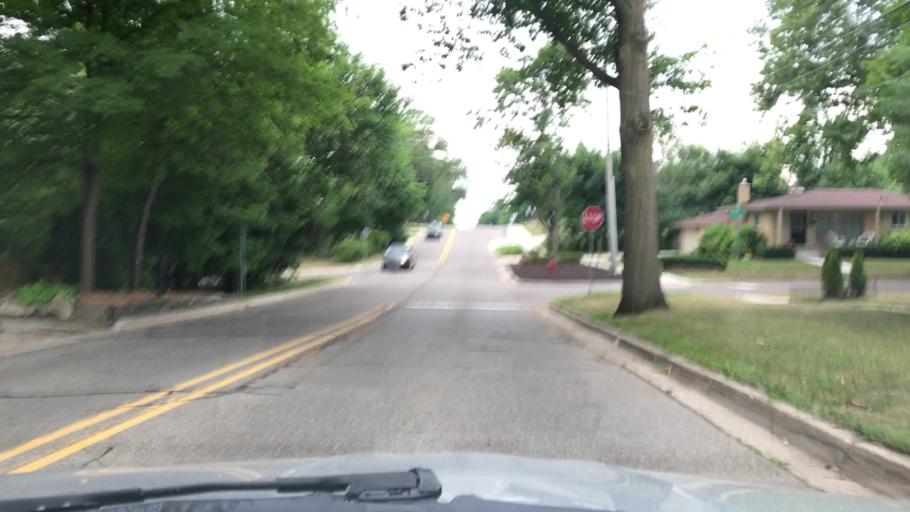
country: US
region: Michigan
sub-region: Wayne County
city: Northville
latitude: 42.4417
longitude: -83.4835
